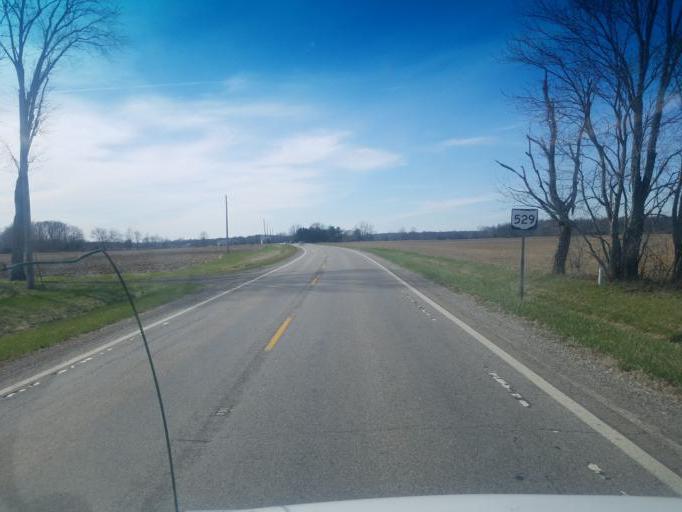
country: US
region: Ohio
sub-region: Morrow County
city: Cardington
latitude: 40.5135
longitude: -82.9200
